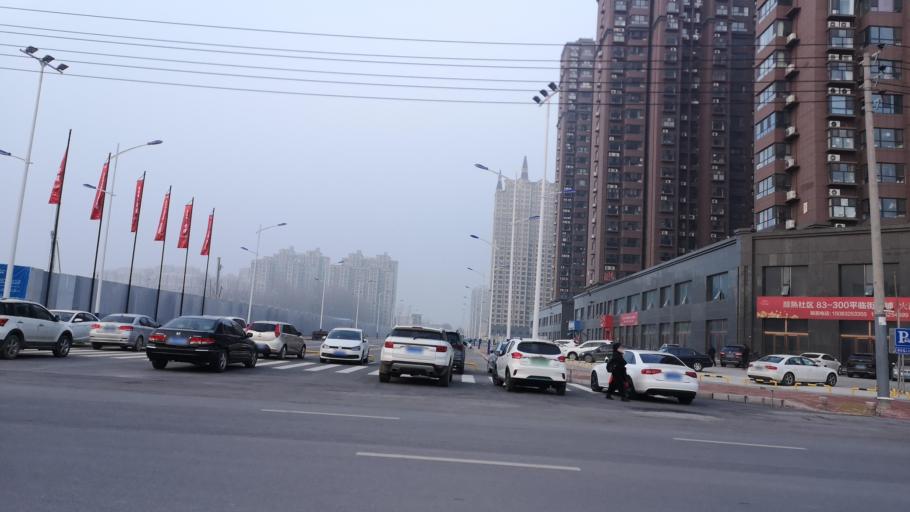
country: CN
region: Henan Sheng
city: Zhongyuanlu
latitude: 35.7473
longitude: 115.0594
